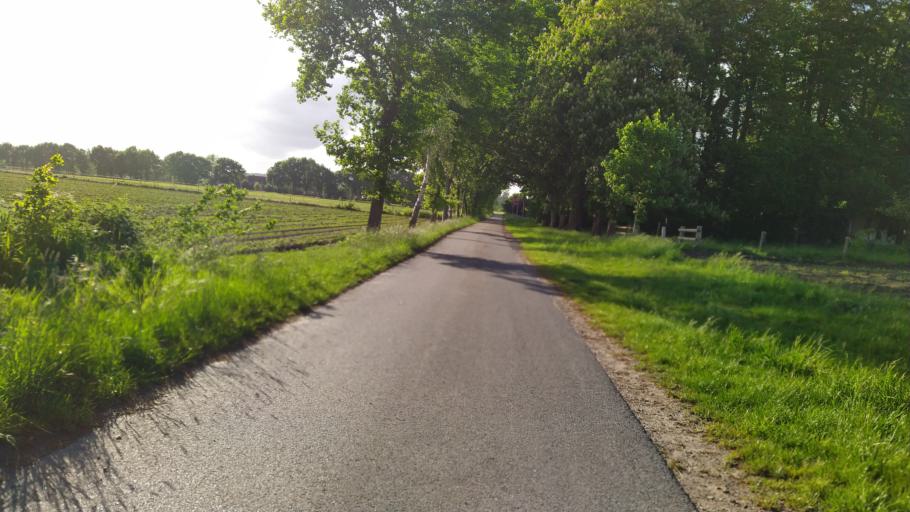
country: DE
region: Lower Saxony
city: Farven
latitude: 53.4493
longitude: 9.2800
